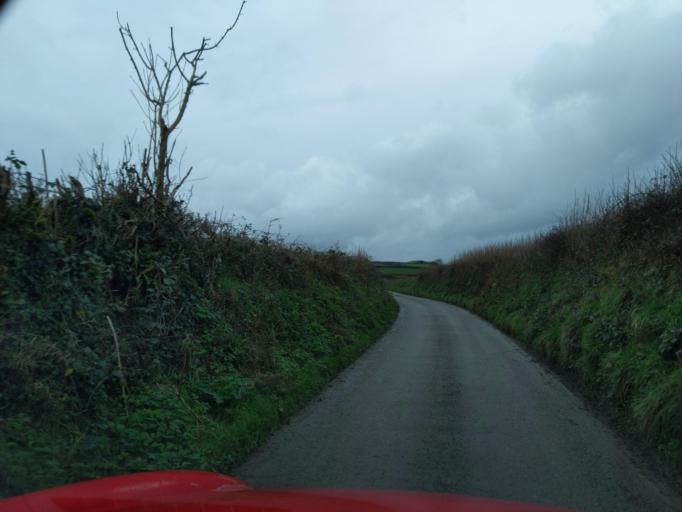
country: GB
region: England
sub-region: Cornwall
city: Duloe
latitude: 50.3474
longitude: -4.5360
